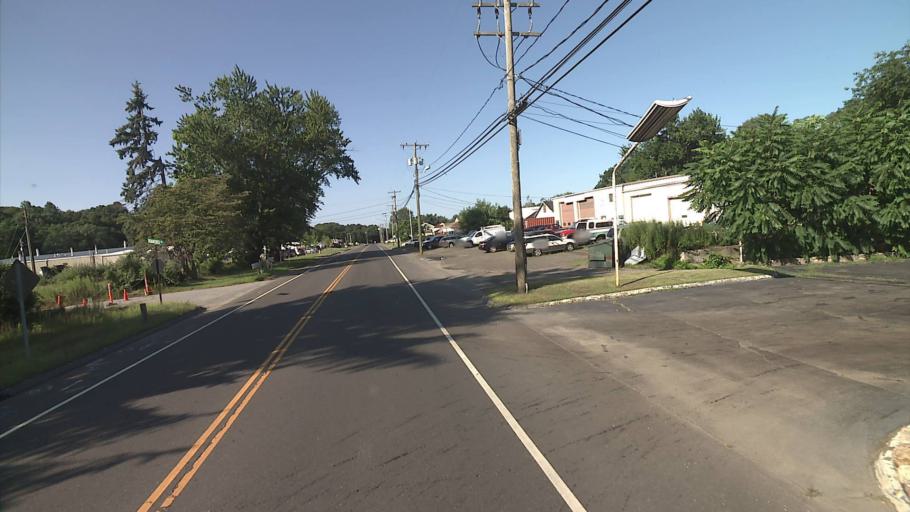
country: US
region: Connecticut
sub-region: Middlesex County
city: Old Saybrook Center
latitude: 41.3077
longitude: -72.3691
